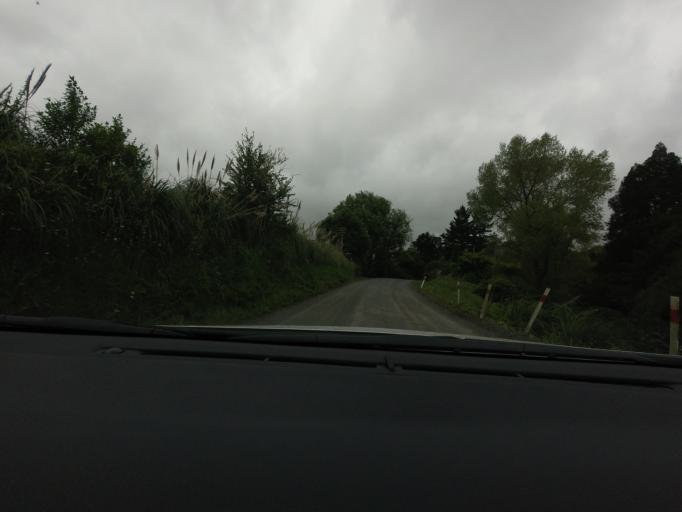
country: NZ
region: Auckland
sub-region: Auckland
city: Warkworth
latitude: -36.4788
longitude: 174.5561
